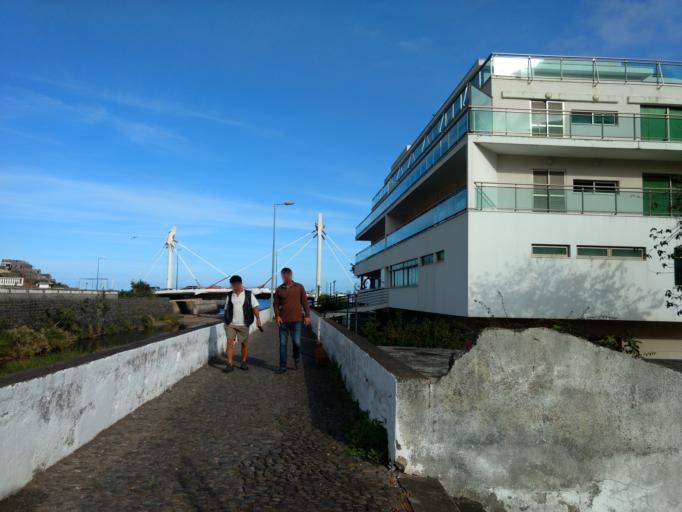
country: PT
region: Madeira
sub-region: Machico
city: Machico
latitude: 32.7186
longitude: -16.7645
